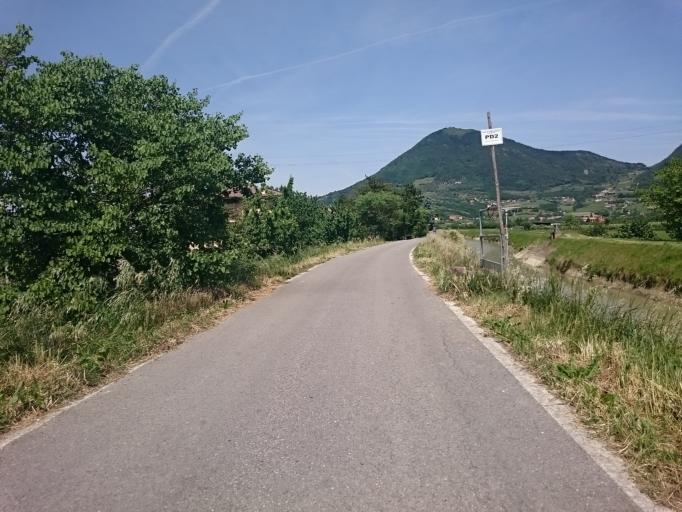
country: IT
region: Veneto
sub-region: Provincia di Padova
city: Vo
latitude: 45.3449
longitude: 11.6252
